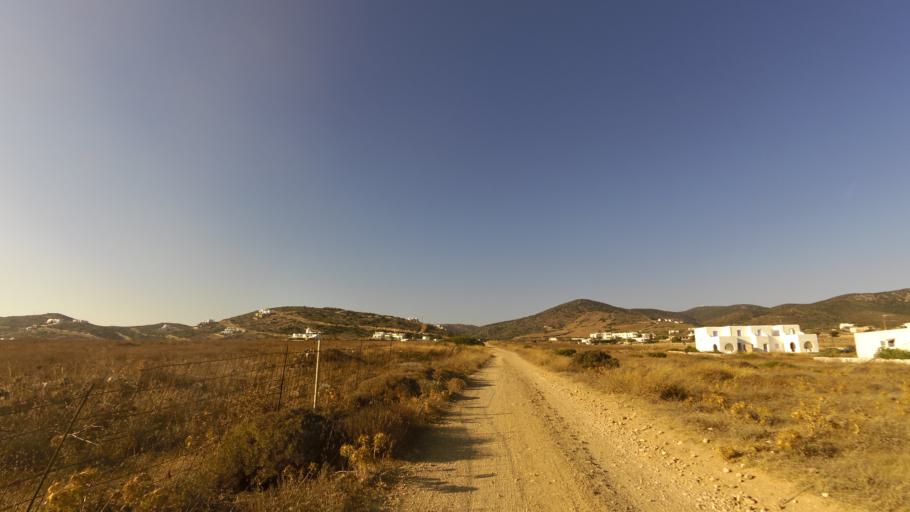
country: GR
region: South Aegean
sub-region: Nomos Kykladon
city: Antiparos
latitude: 36.9754
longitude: 25.0269
